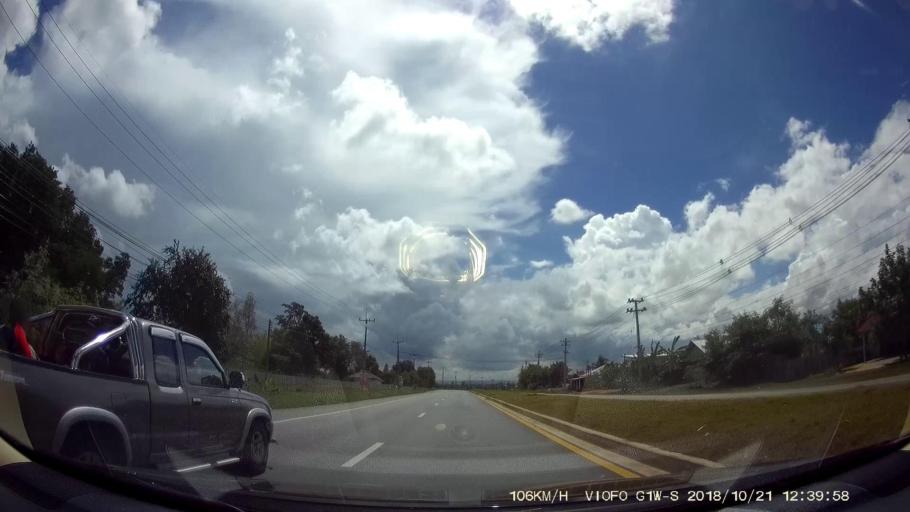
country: TH
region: Nakhon Ratchasima
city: Amphoe Sikhiu
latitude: 15.0313
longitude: 101.6980
